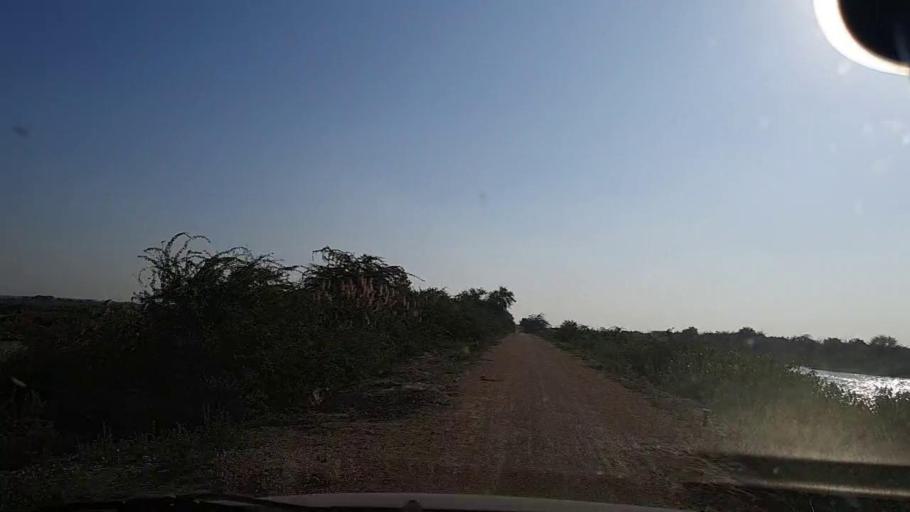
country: PK
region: Sindh
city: Chuhar Jamali
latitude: 24.5573
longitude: 68.0381
